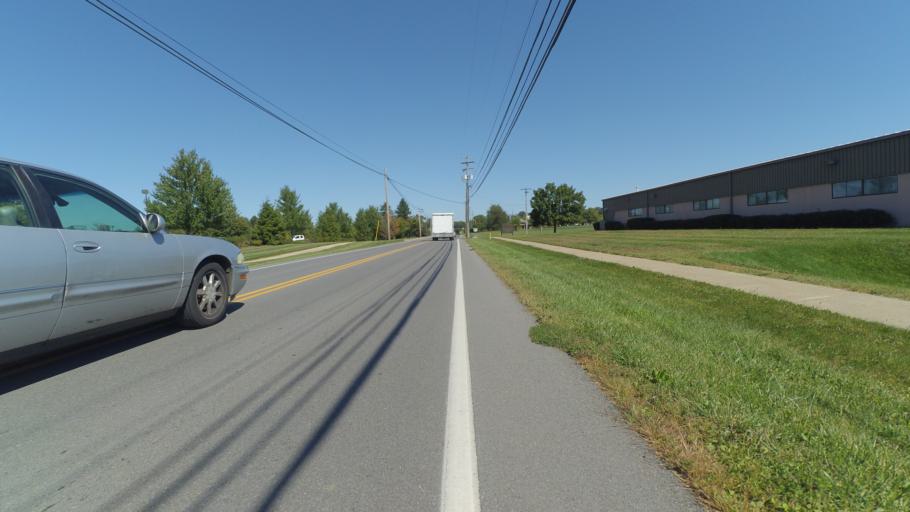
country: US
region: Pennsylvania
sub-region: Centre County
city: Park Forest Village
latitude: 40.7772
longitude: -77.8989
